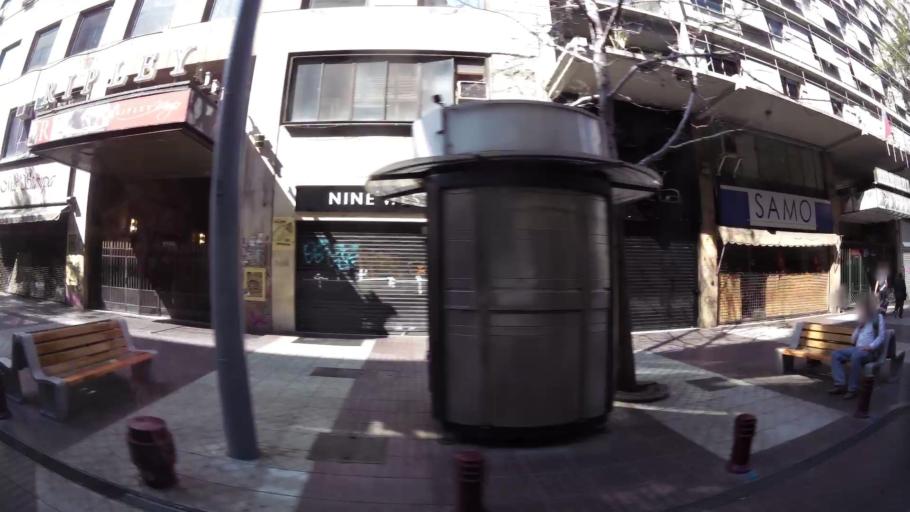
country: CL
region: Santiago Metropolitan
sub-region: Provincia de Santiago
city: Santiago
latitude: -33.4400
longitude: -70.6495
